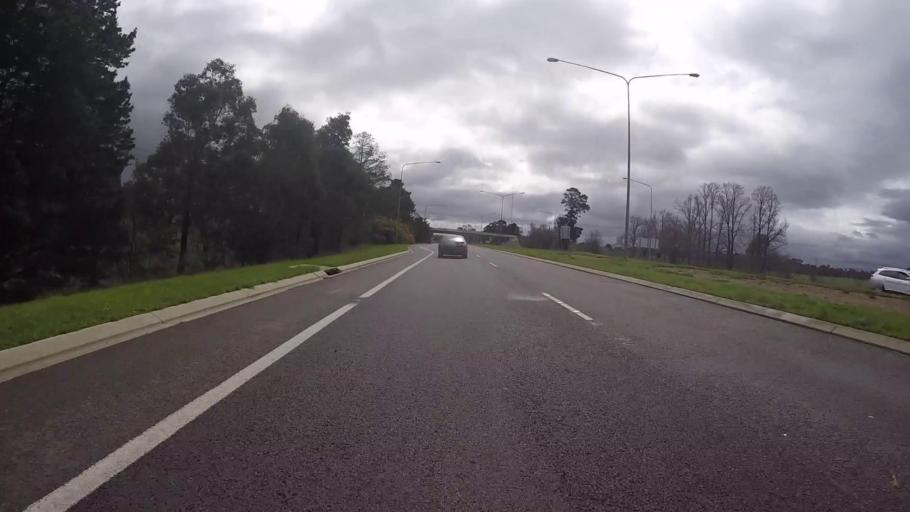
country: AU
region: Australian Capital Territory
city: Kaleen
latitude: -35.2282
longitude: 149.1233
